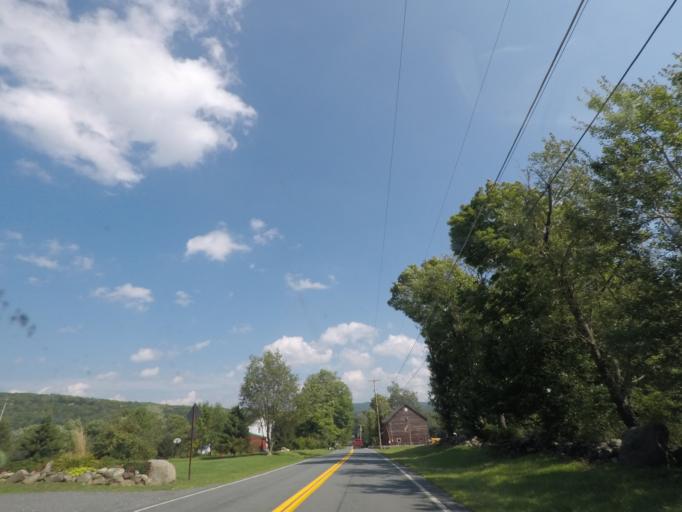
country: US
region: New York
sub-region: Rensselaer County
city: Poestenkill
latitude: 42.6824
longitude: -73.5205
